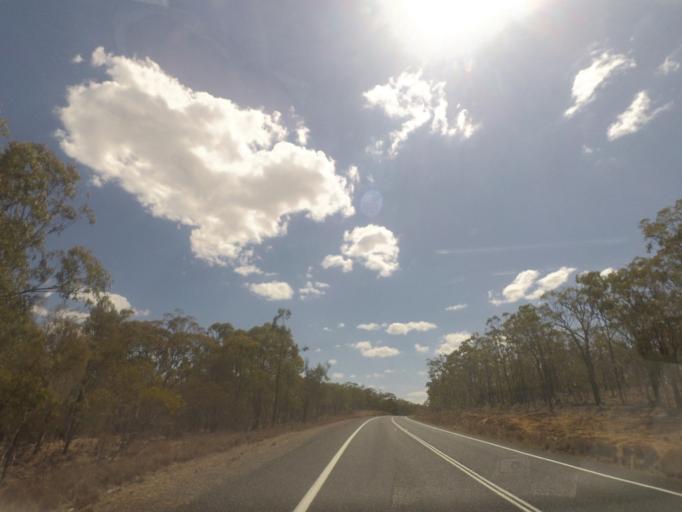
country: AU
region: Queensland
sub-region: Southern Downs
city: Warwick
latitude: -28.1622
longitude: 151.6825
